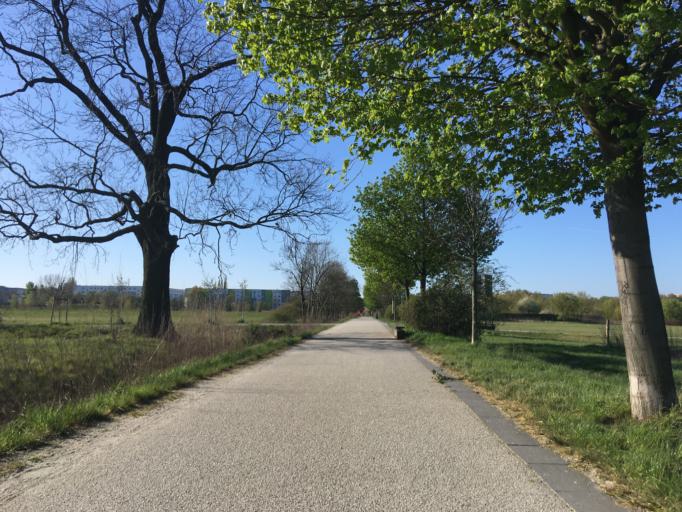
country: DE
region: Berlin
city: Wartenberg
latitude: 52.5813
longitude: 13.5037
